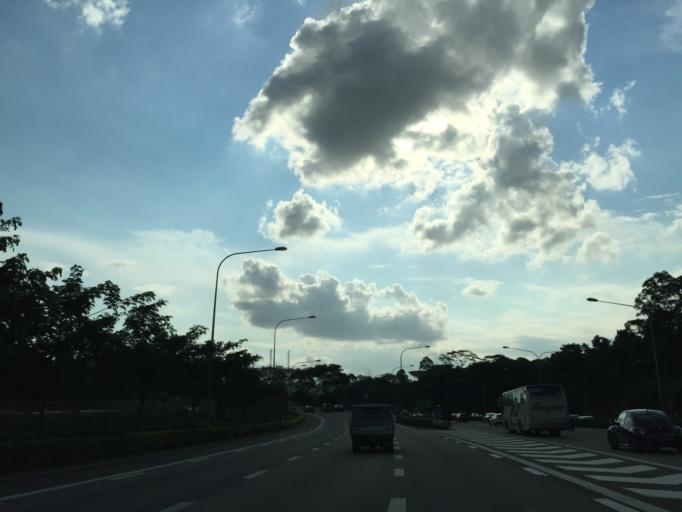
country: SG
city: Singapore
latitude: 1.3487
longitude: 103.7962
